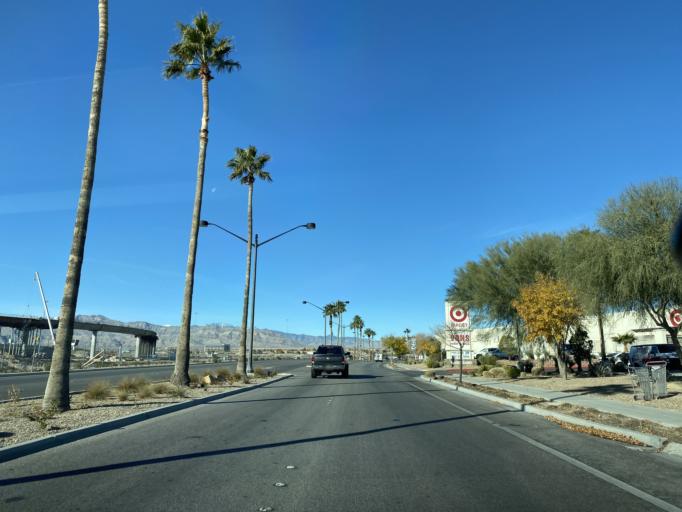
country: US
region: Nevada
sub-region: Clark County
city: Las Vegas
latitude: 36.2790
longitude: -115.2632
